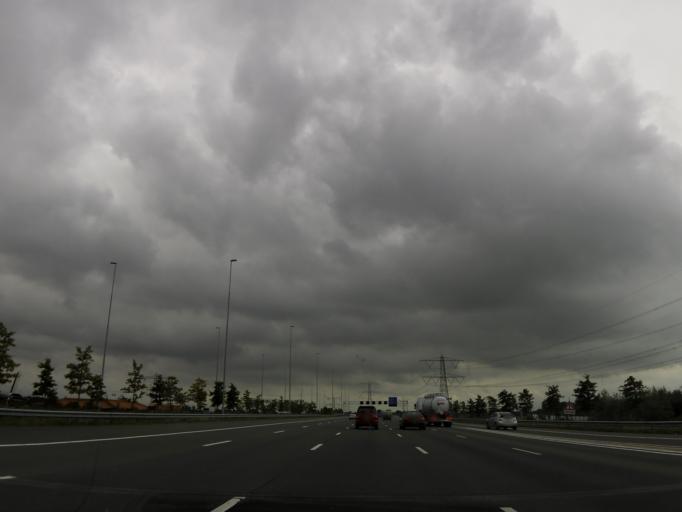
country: NL
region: Utrecht
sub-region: Stichtse Vecht
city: Breukelen
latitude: 52.1720
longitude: 4.9867
